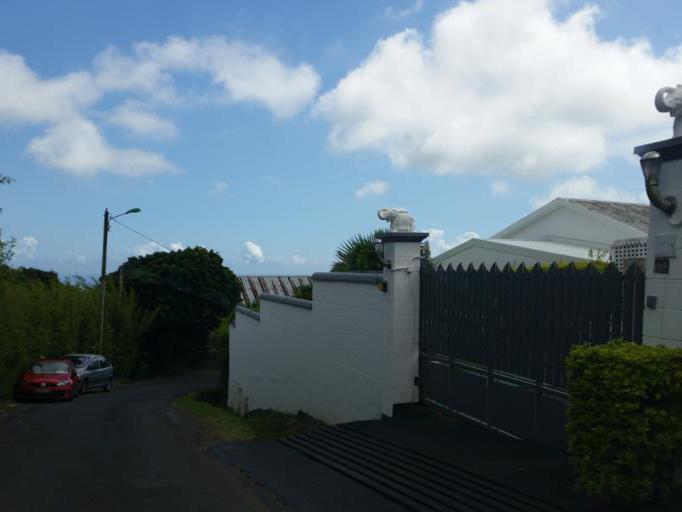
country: RE
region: Reunion
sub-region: Reunion
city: Sainte-Marie
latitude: -20.9372
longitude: 55.5284
